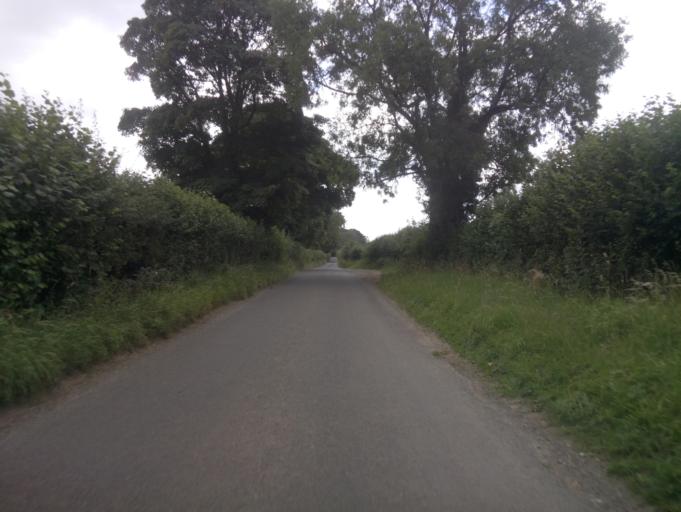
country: GB
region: England
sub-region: Gloucestershire
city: Chalford
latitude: 51.7609
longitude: -2.0869
